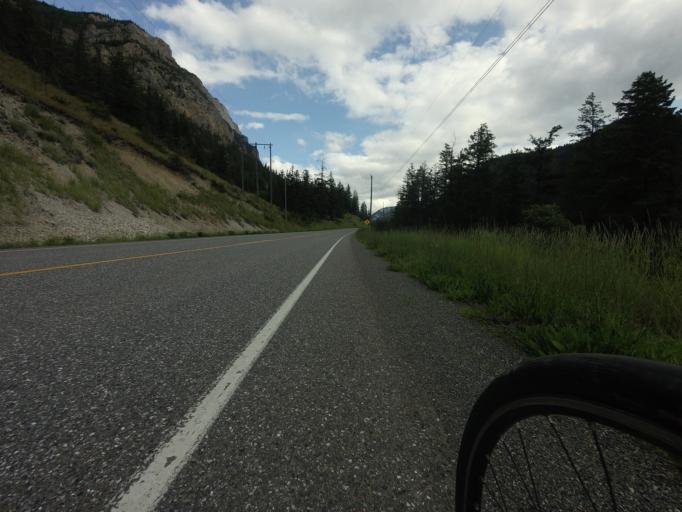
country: CA
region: British Columbia
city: Lillooet
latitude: 50.8607
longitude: -121.7266
